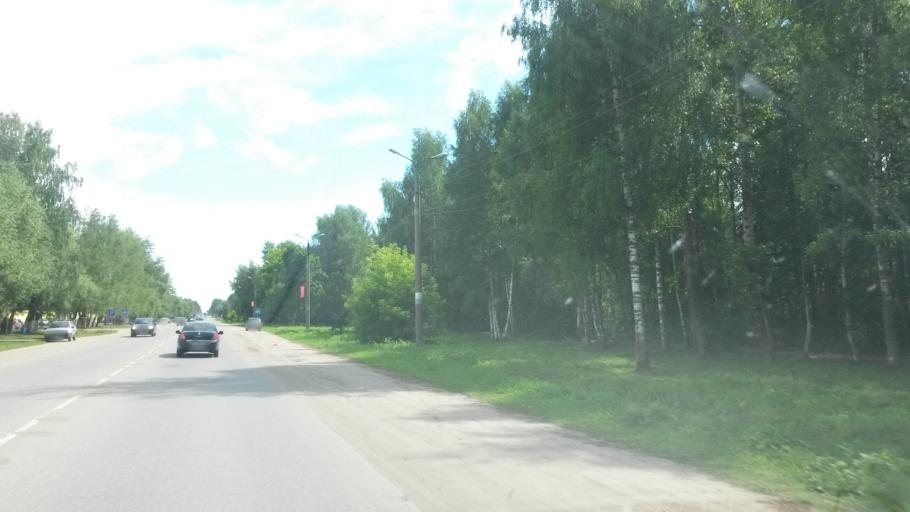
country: RU
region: Ivanovo
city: Zavolzhsk
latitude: 57.4865
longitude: 42.1428
